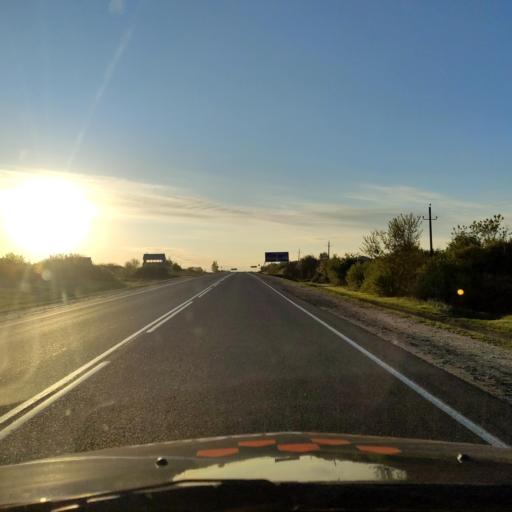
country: RU
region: Orjol
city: Livny
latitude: 52.4493
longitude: 37.6219
